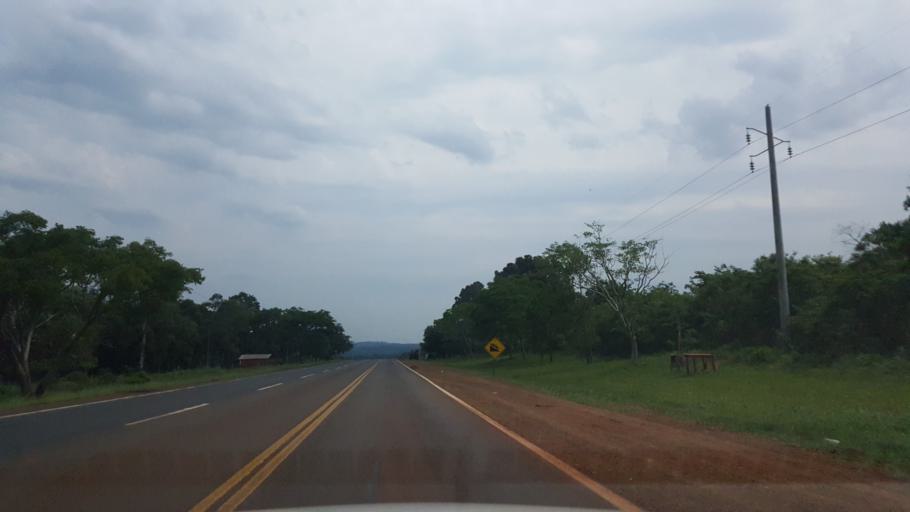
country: AR
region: Misiones
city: Capiovi
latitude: -26.9468
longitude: -55.0874
